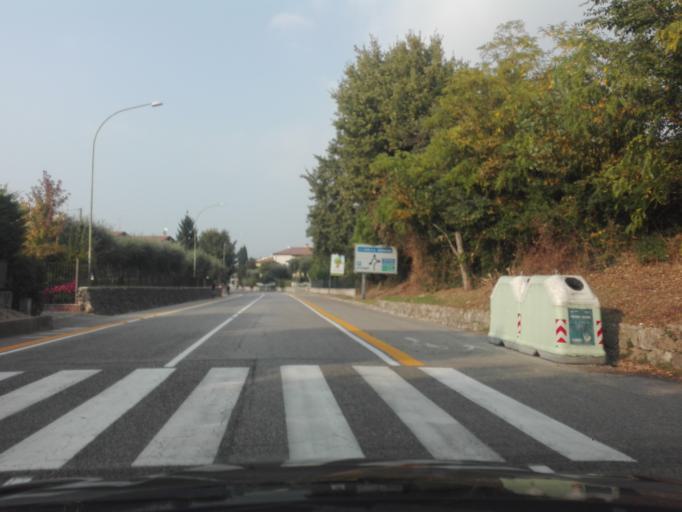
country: IT
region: Veneto
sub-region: Provincia di Verona
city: Lazise
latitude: 45.5003
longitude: 10.7371
